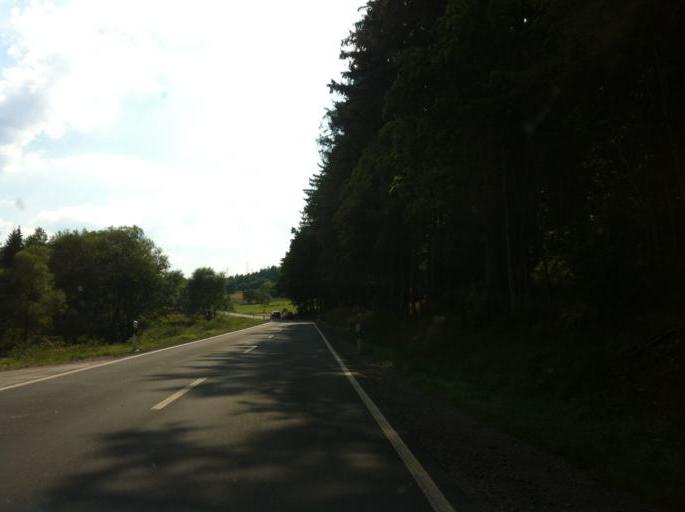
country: DE
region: Thuringia
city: Mohrenbach
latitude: 50.6182
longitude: 10.9951
